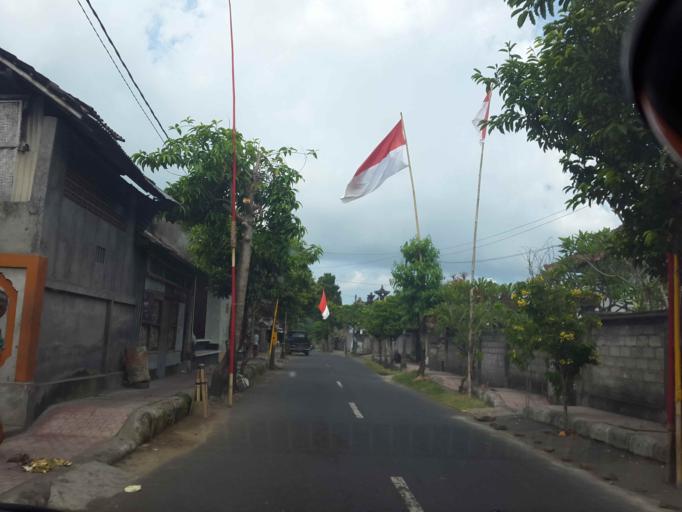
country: ID
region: Bali
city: Klungkung
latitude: -8.5320
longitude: 115.3837
